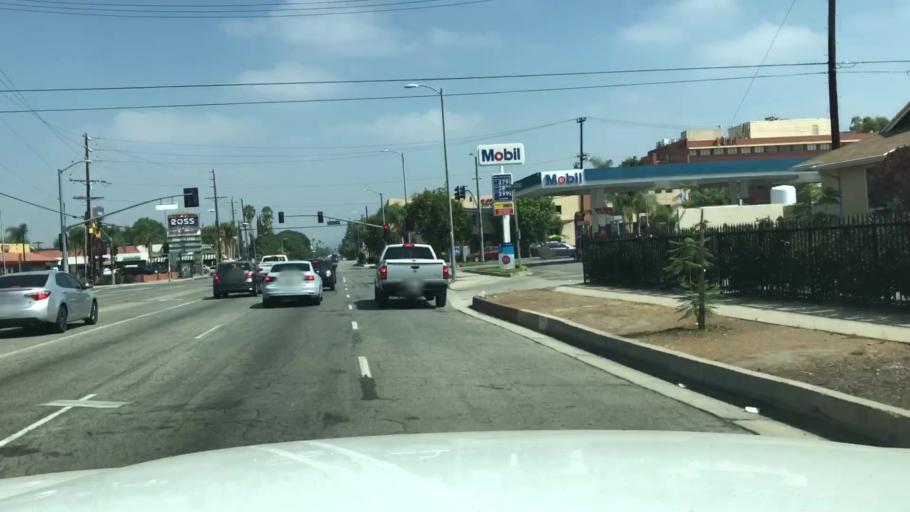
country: US
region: California
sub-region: Los Angeles County
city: Northridge
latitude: 34.1859
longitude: -118.5535
